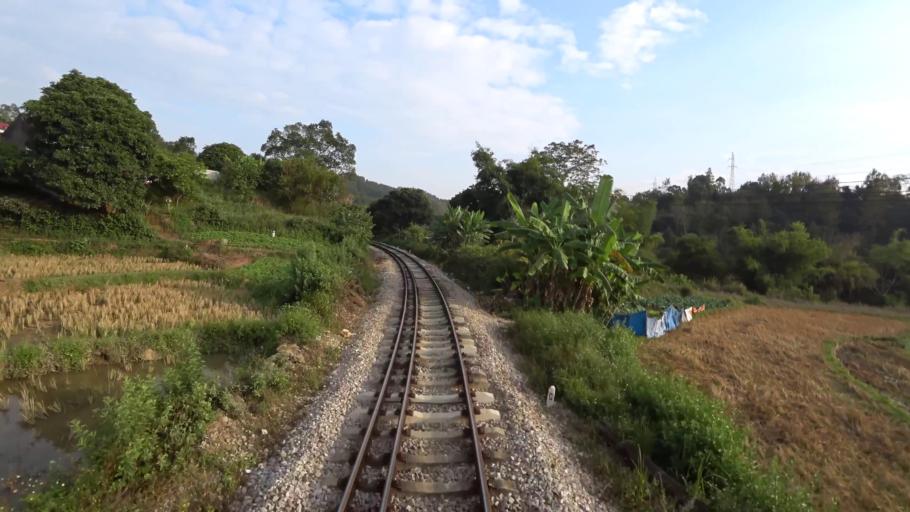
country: VN
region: Lang Son
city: Thi Tran Cao Loc
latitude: 21.9279
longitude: 106.7056
